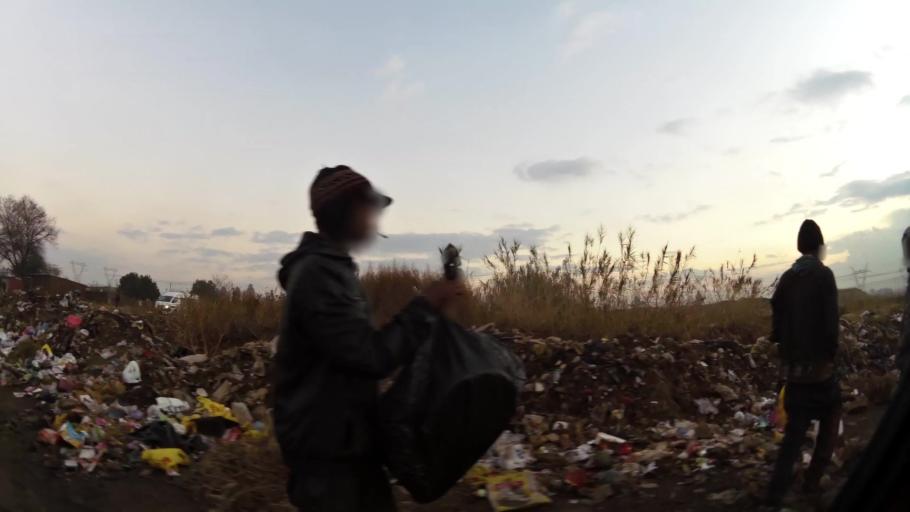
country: ZA
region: Gauteng
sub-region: City of Johannesburg Metropolitan Municipality
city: Orange Farm
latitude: -26.5506
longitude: 27.8322
